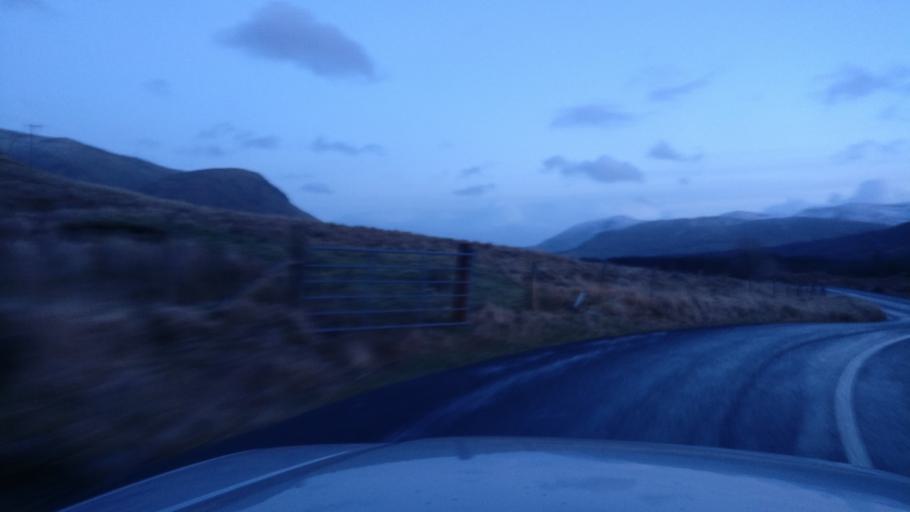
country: IE
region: Connaught
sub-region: Maigh Eo
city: Westport
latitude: 53.5578
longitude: -9.6445
